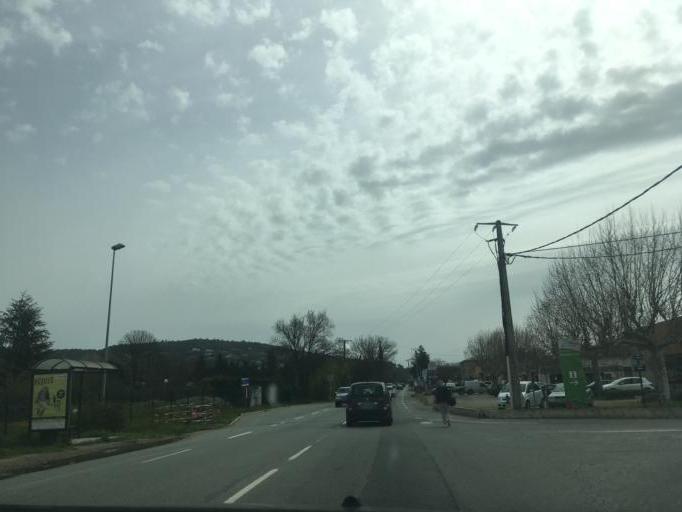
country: FR
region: Provence-Alpes-Cote d'Azur
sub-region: Departement du Var
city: Montauroux
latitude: 43.6049
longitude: 6.7700
